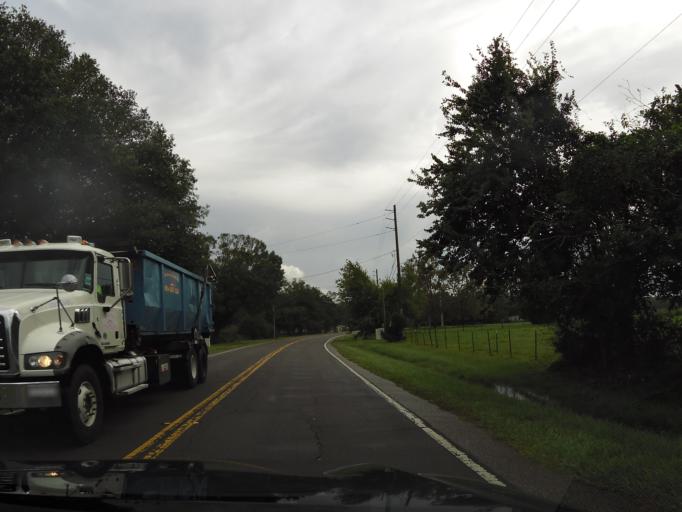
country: US
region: Florida
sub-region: Duval County
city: Baldwin
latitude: 30.3212
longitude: -81.8951
